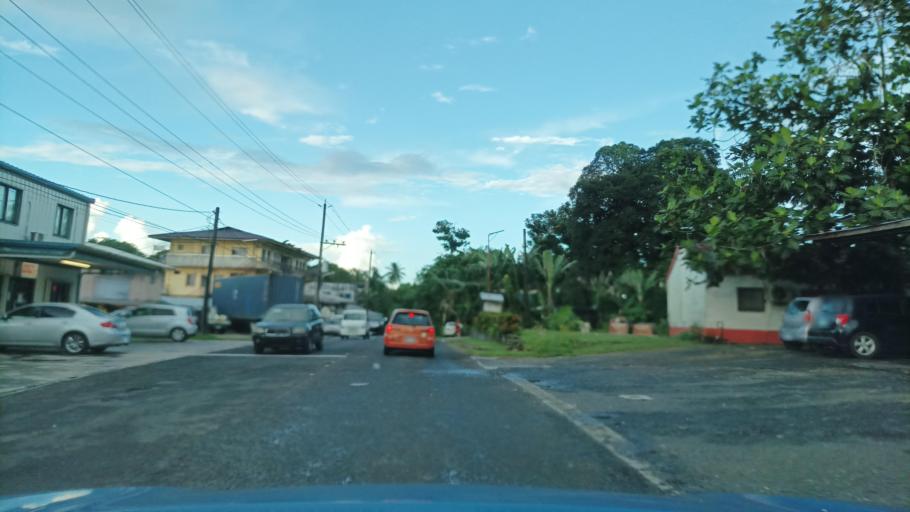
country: FM
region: Pohnpei
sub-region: Kolonia Municipality
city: Kolonia Town
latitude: 6.9573
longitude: 158.2060
